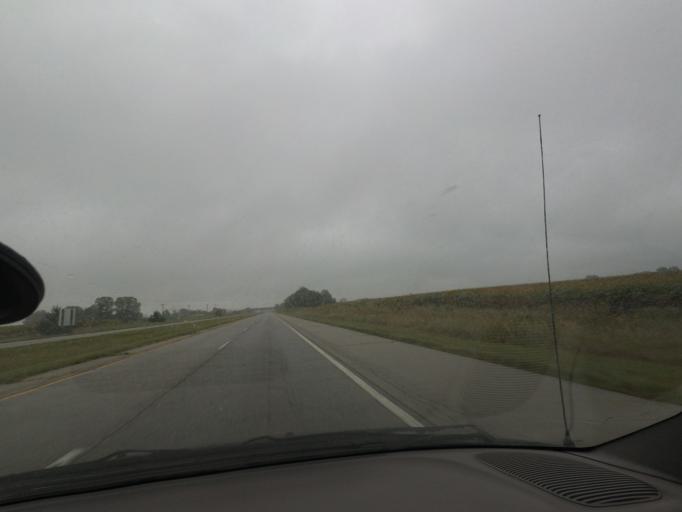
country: US
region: Illinois
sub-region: Pike County
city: Barry
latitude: 39.6970
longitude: -91.0124
